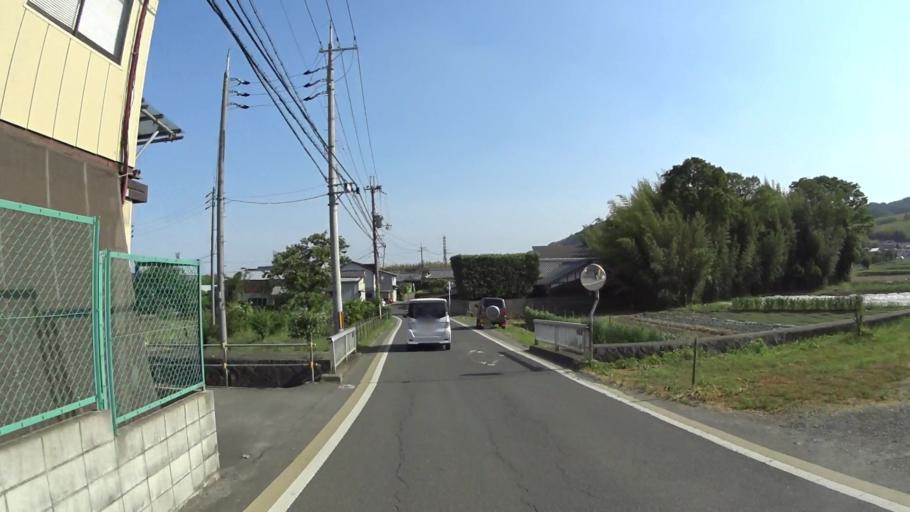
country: JP
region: Kyoto
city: Muko
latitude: 34.9498
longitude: 135.6772
